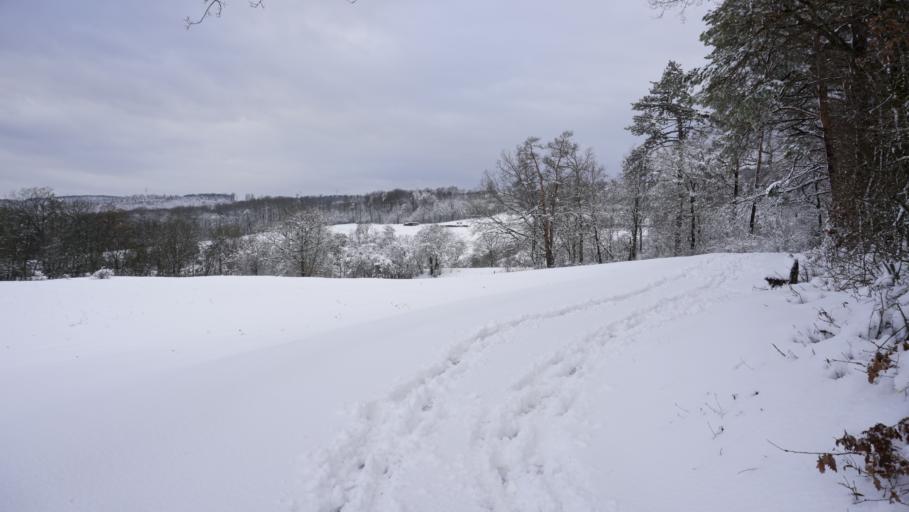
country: DE
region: Baden-Wuerttemberg
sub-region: Karlsruhe Region
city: Mosbach
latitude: 49.3808
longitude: 9.1663
